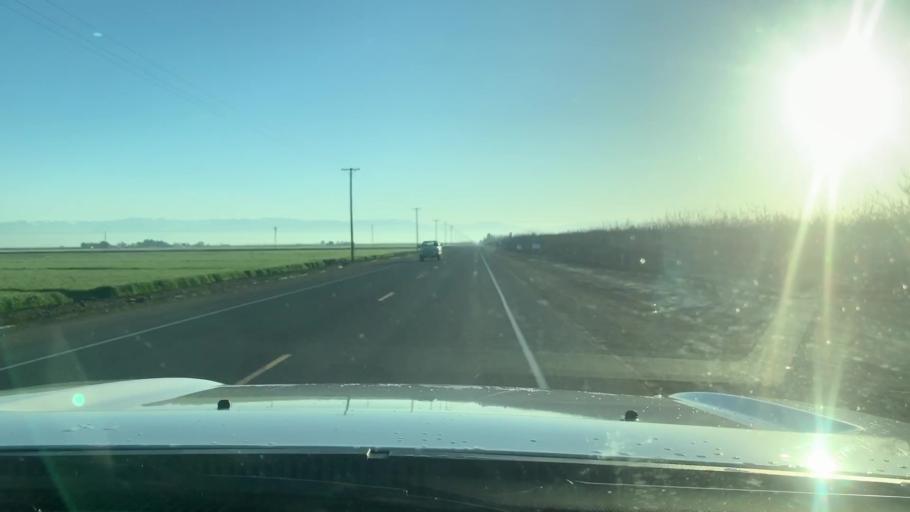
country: US
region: California
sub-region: Kings County
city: Corcoran
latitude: 36.2110
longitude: -119.5149
